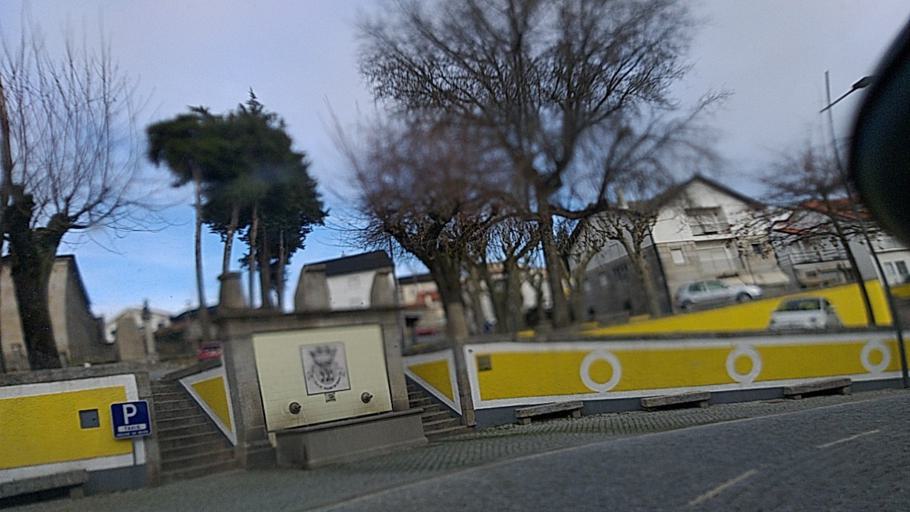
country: PT
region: Guarda
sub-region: Aguiar da Beira
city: Aguiar da Beira
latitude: 40.8173
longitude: -7.5436
